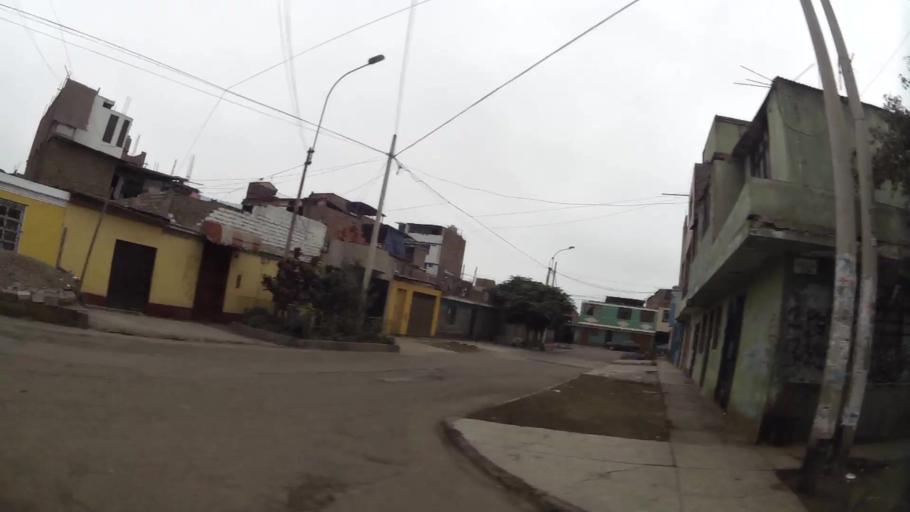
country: PE
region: Lima
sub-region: Lima
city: Surco
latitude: -12.1547
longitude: -76.9670
